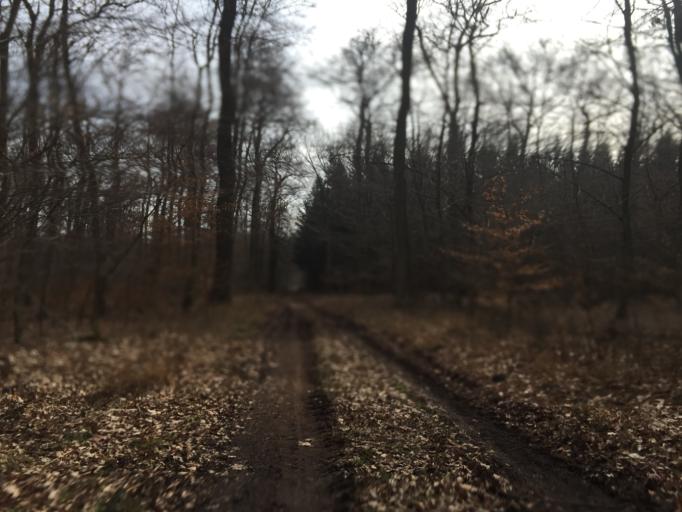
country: DE
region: Hesse
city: Viernheim
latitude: 49.5702
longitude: 8.5819
